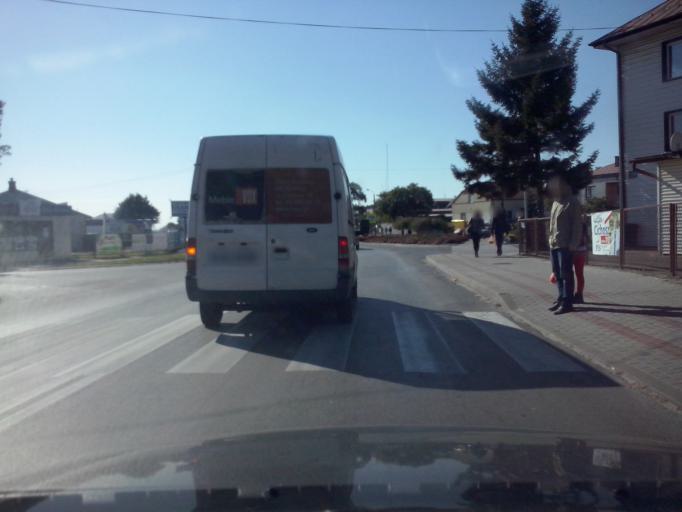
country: PL
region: Lublin Voivodeship
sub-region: Powiat bilgorajski
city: Bilgoraj
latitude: 50.5337
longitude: 22.7219
